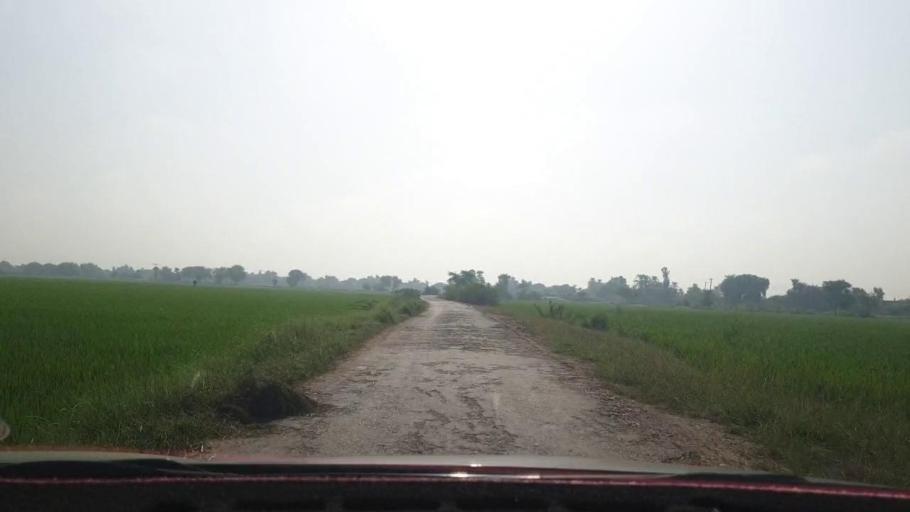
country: PK
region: Sindh
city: Nasirabad
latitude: 27.4555
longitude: 67.9587
